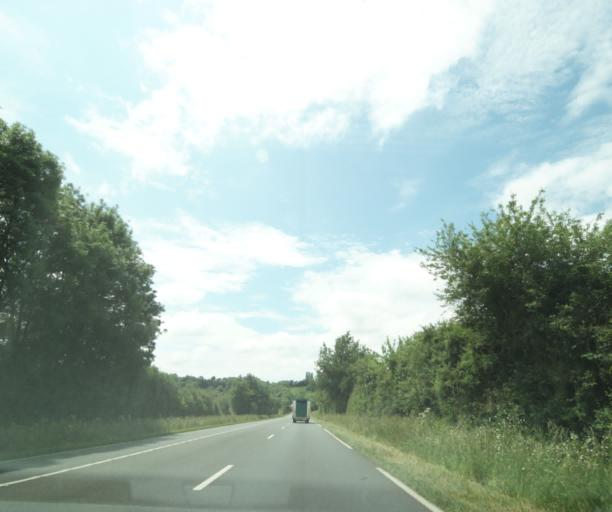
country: FR
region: Poitou-Charentes
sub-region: Departement des Deux-Sevres
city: Champdeniers-Saint-Denis
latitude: 46.4841
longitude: -0.3560
